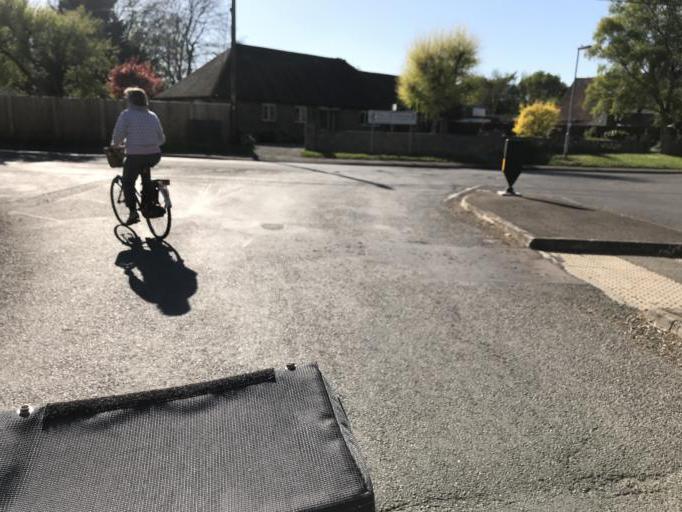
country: GB
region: England
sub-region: Cambridgeshire
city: Fulbourn
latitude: 52.2031
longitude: 0.1901
